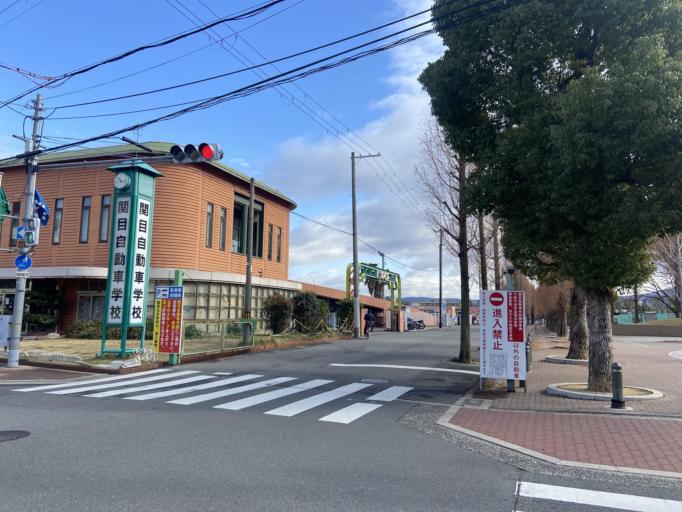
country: JP
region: Osaka
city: Moriguchi
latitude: 34.7117
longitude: 135.5628
